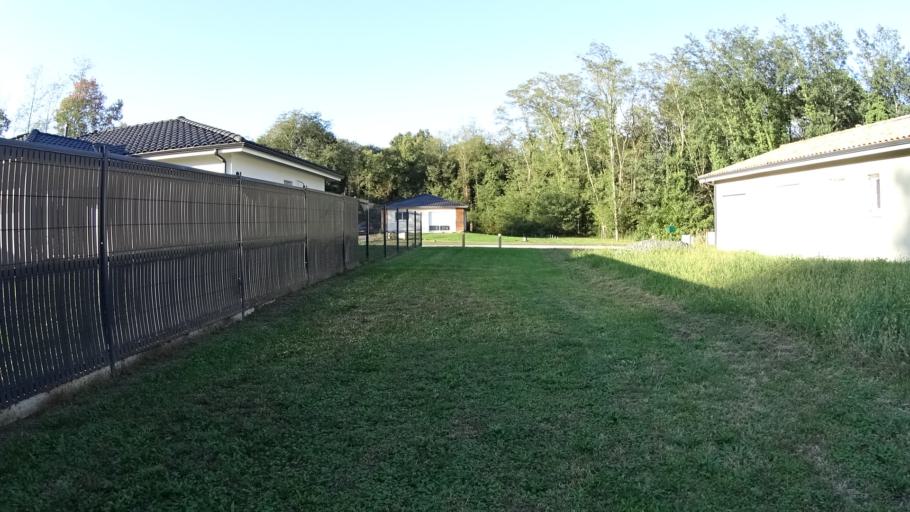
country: FR
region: Aquitaine
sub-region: Departement des Landes
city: Saint-Paul-les-Dax
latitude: 43.7419
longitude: -1.0469
